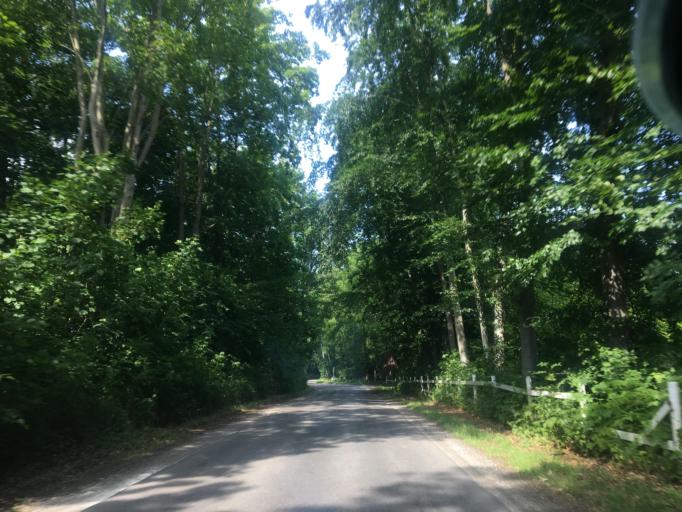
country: DK
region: Zealand
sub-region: Vordingborg Kommune
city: Praesto
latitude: 55.1829
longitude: 12.0810
